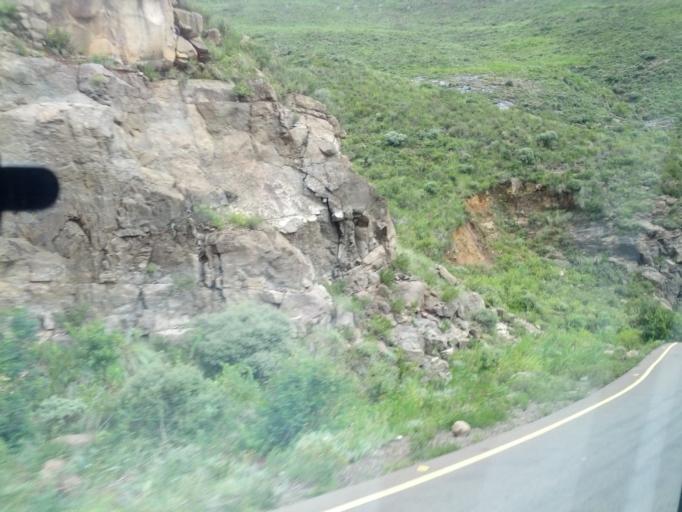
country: LS
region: Butha-Buthe
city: Butha-Buthe
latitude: -29.0597
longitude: 28.3592
